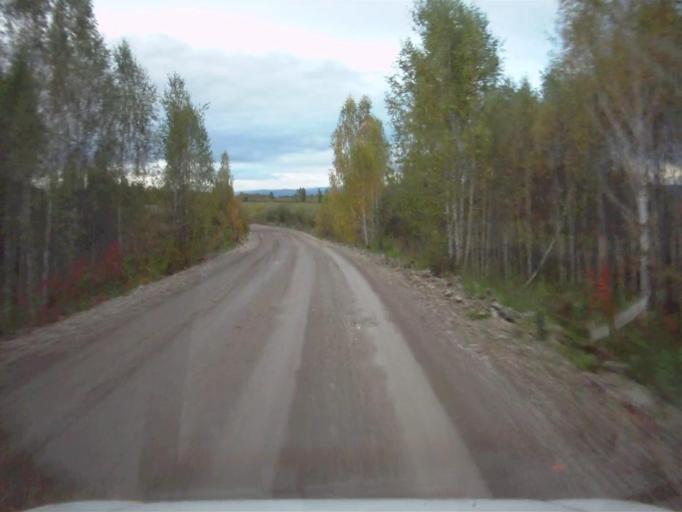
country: RU
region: Sverdlovsk
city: Mikhaylovsk
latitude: 56.1957
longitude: 59.1987
